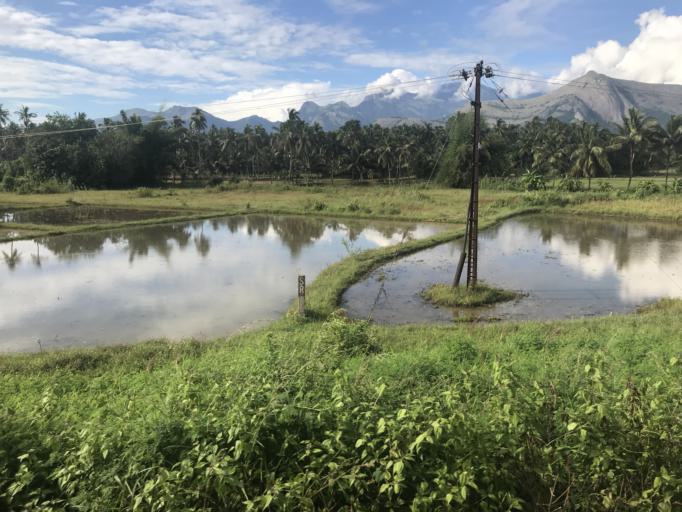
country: IN
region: Kerala
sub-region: Palakkad district
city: Palakkad
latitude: 10.8084
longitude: 76.6542
